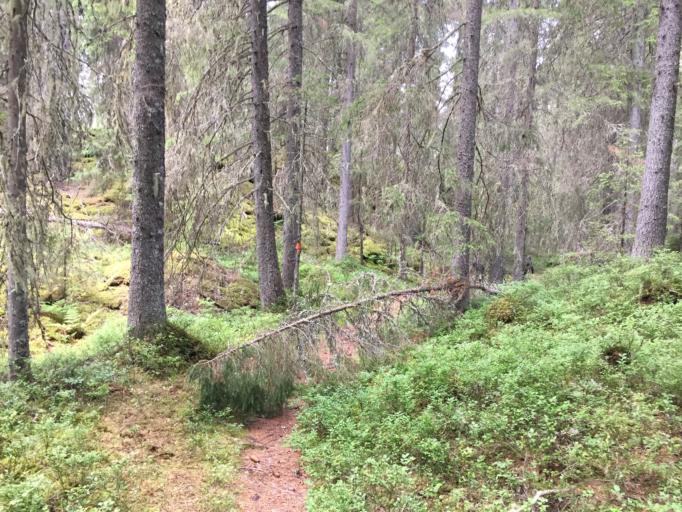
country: SE
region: Dalarna
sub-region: Malung-Saelens kommun
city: Malung
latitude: 60.6394
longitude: 13.7757
